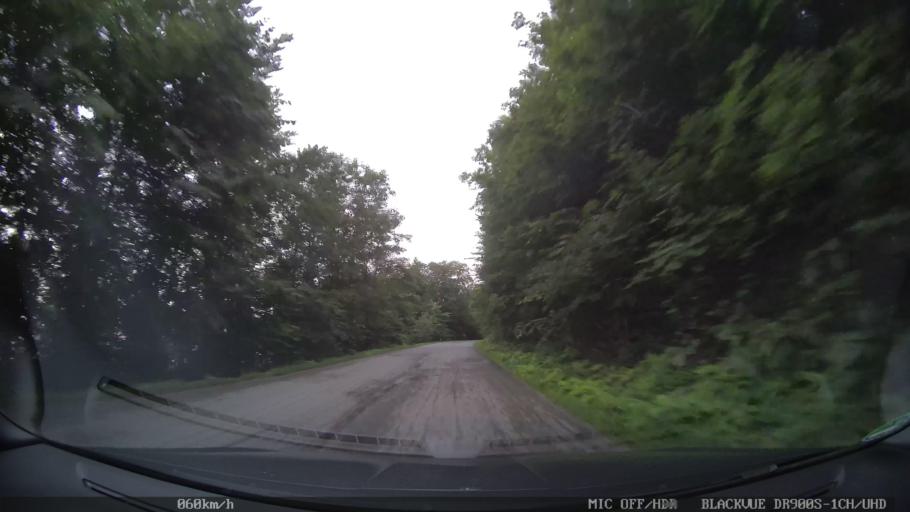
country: HR
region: Primorsko-Goranska
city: Vrbovsko
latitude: 45.1831
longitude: 14.9892
